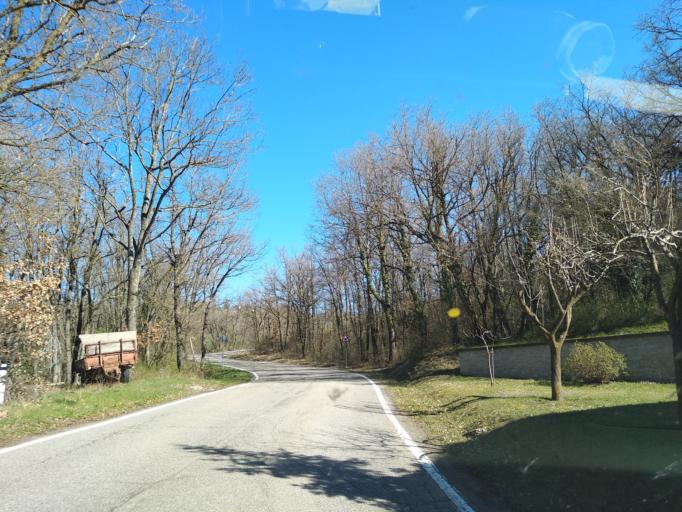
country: IT
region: Emilia-Romagna
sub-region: Provincia di Reggio Emilia
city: Castelnovo ne'Monti
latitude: 44.4022
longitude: 10.3972
